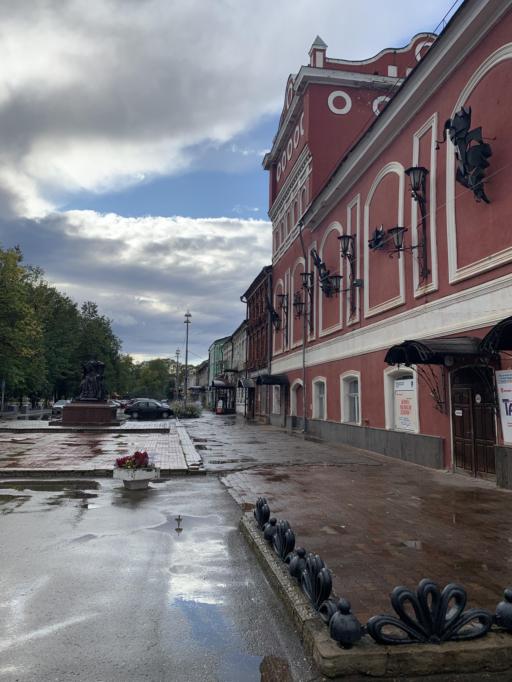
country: RU
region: Tverskaya
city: Vyshniy Volochek
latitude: 57.5848
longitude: 34.5599
